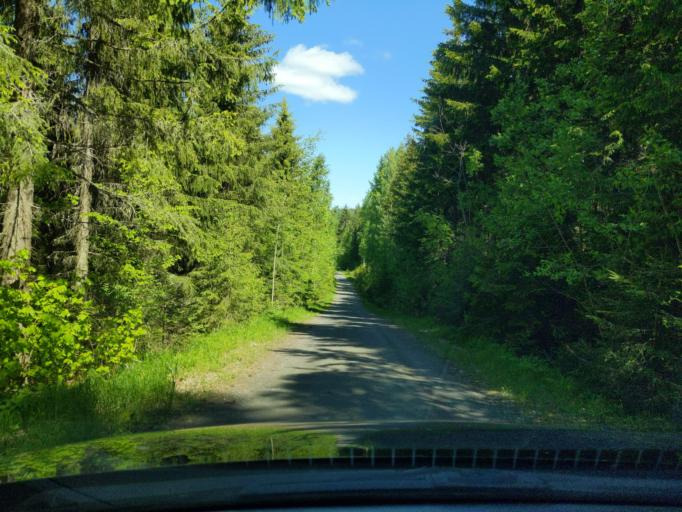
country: FI
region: Paijanne Tavastia
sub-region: Lahti
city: Lahti
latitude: 61.0552
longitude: 25.6973
